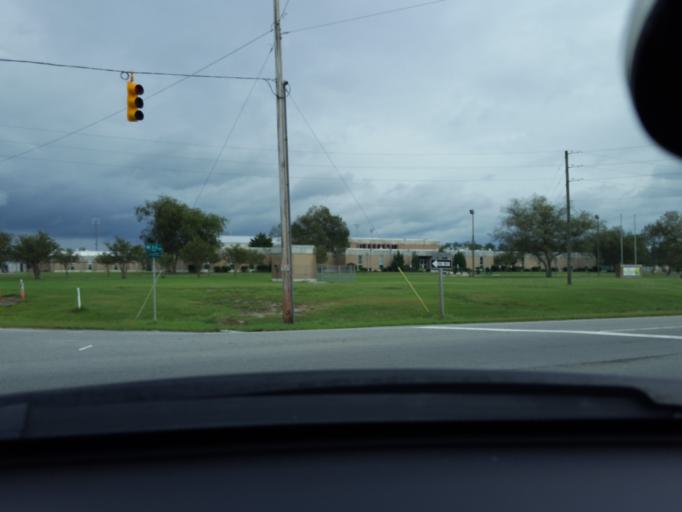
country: US
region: North Carolina
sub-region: Pitt County
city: Ayden
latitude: 35.4312
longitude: -77.4334
